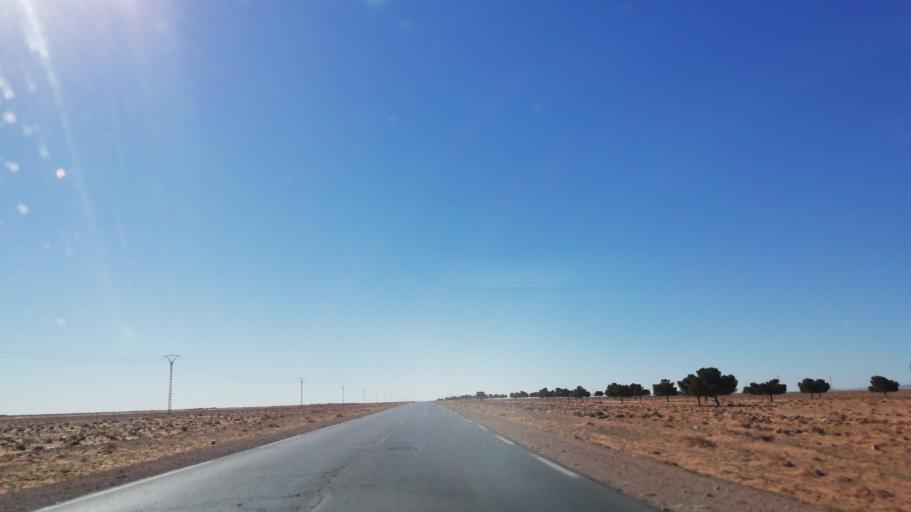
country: DZ
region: Saida
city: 'Ain el Hadjar
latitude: 33.9864
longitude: 0.0326
